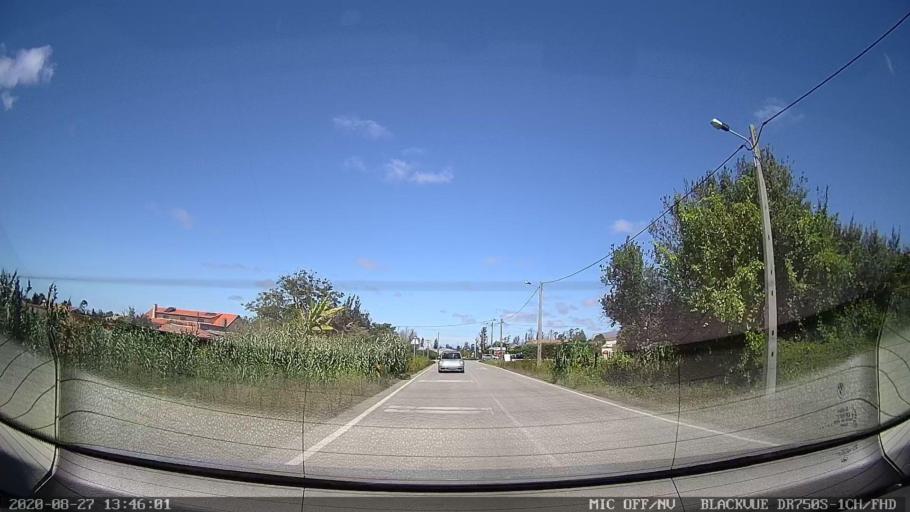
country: PT
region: Coimbra
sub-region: Mira
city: Mira
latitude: 40.3992
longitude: -8.7354
